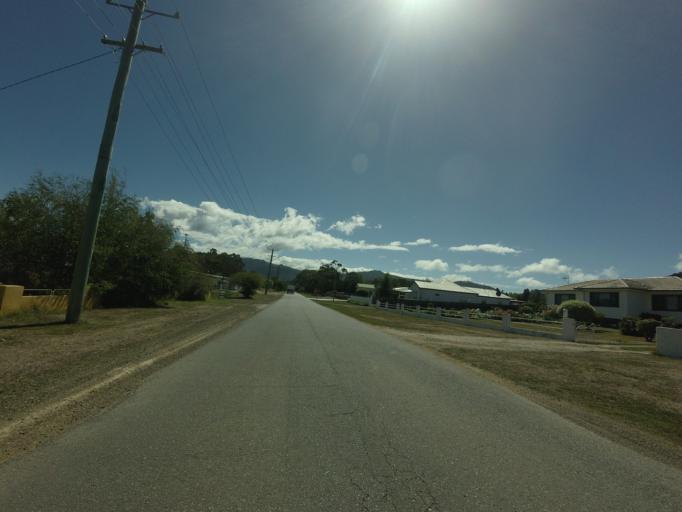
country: AU
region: Tasmania
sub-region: Break O'Day
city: St Helens
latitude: -41.5869
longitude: 148.1883
